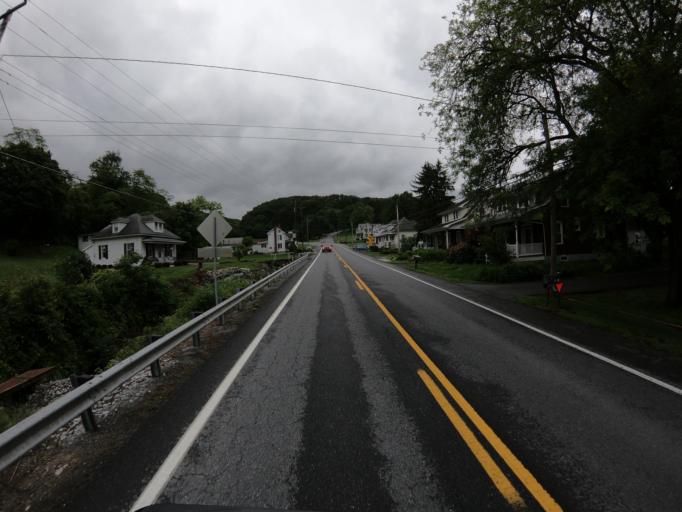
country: US
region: Maryland
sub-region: Washington County
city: Boonsboro
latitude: 39.4920
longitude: -77.6388
